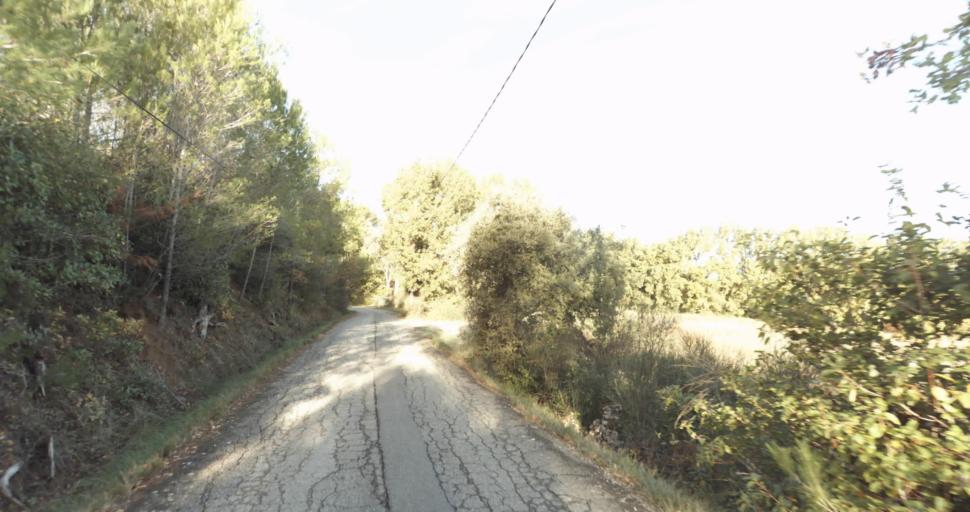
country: FR
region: Provence-Alpes-Cote d'Azur
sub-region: Departement des Bouches-du-Rhone
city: Venelles
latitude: 43.6253
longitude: 5.4641
